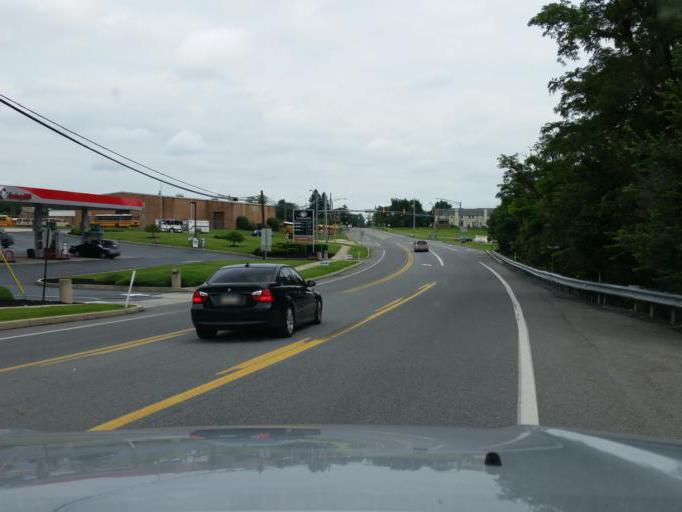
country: US
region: Pennsylvania
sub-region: Dauphin County
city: Colonial Park
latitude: 40.2810
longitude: -76.7997
